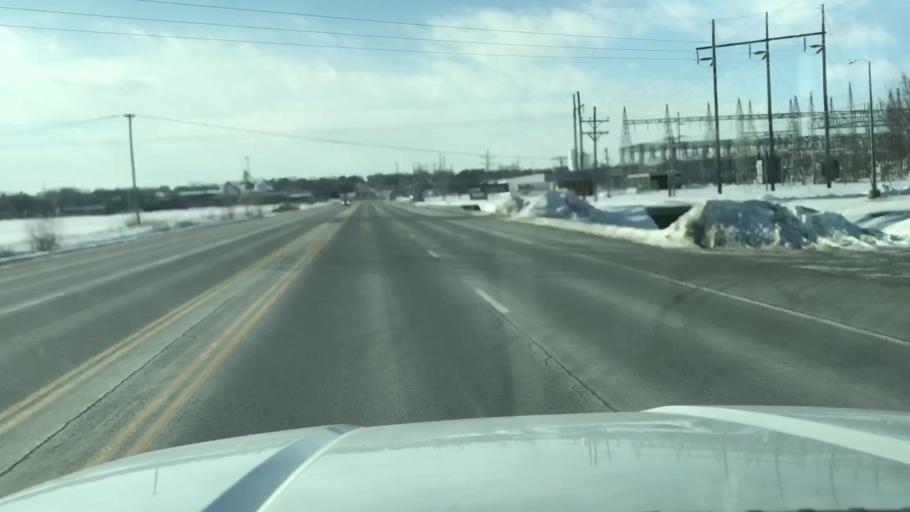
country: US
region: Missouri
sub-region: Nodaway County
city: Maryville
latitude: 40.3451
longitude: -94.8413
